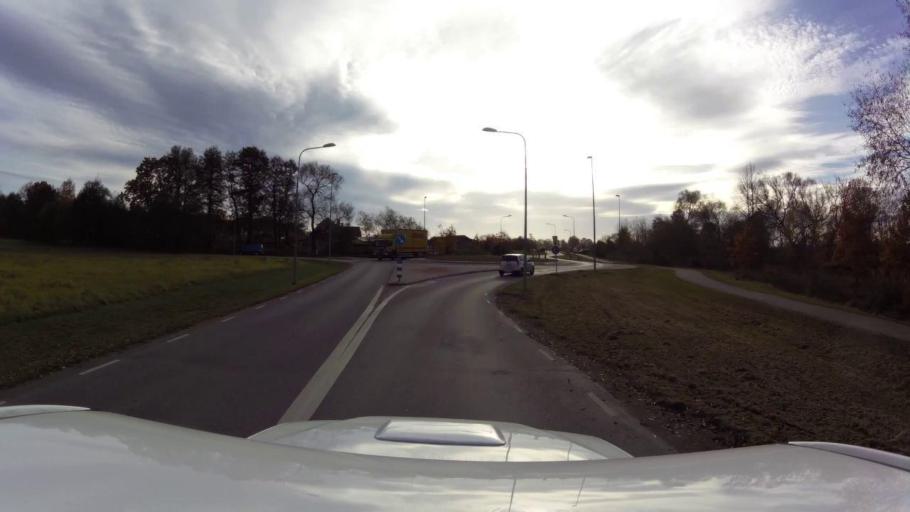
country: SE
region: OEstergoetland
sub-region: Linkopings Kommun
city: Ekangen
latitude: 58.4606
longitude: 15.6402
